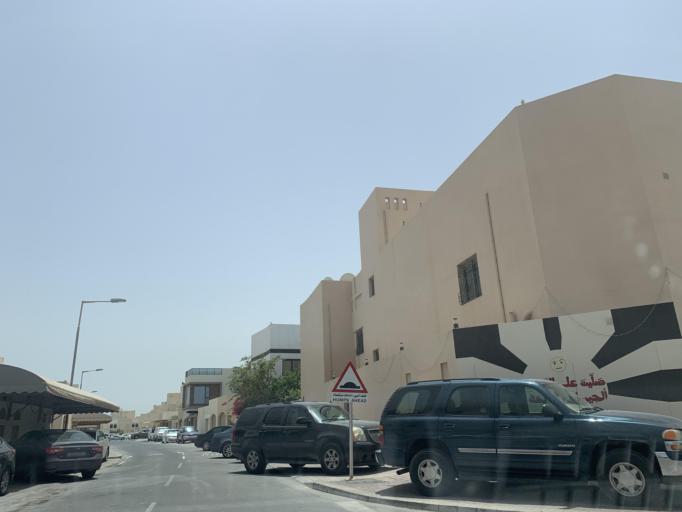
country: BH
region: Northern
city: Sitrah
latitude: 26.1487
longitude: 50.5883
